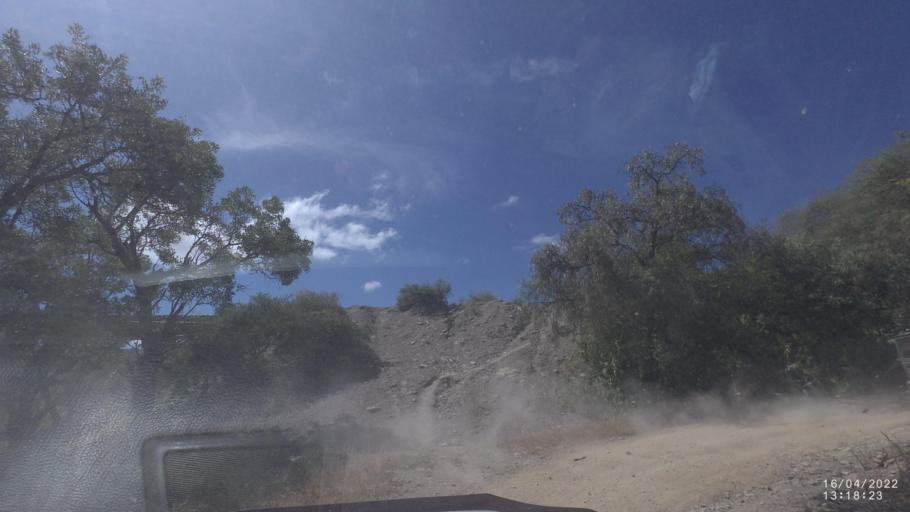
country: BO
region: Cochabamba
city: Mizque
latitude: -17.9864
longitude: -65.6181
